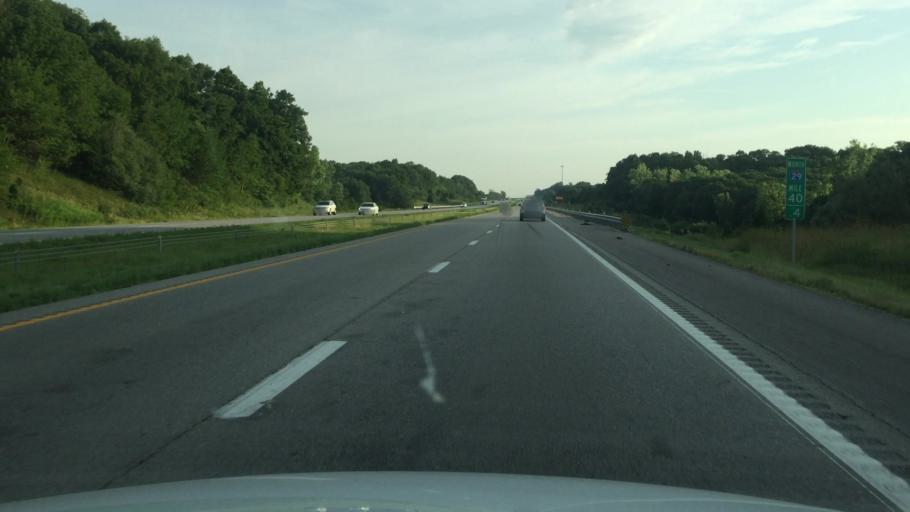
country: US
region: Missouri
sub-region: Buchanan County
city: Saint Joseph
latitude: 39.6675
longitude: -94.7879
